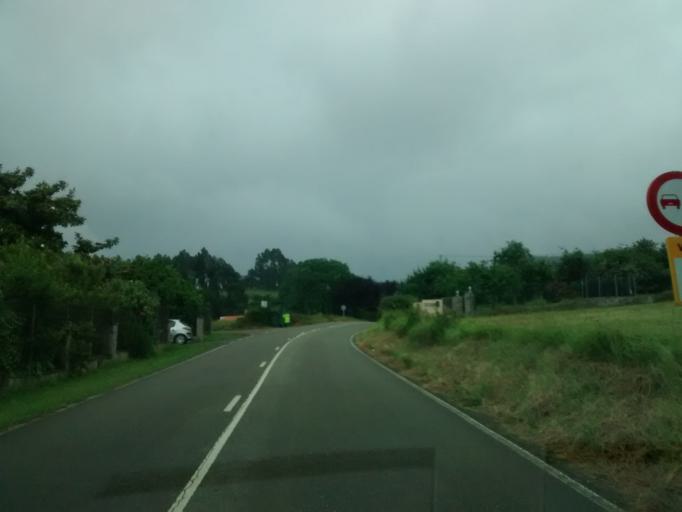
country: ES
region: Asturias
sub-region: Province of Asturias
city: Villaviciosa
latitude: 43.5268
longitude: -5.3737
